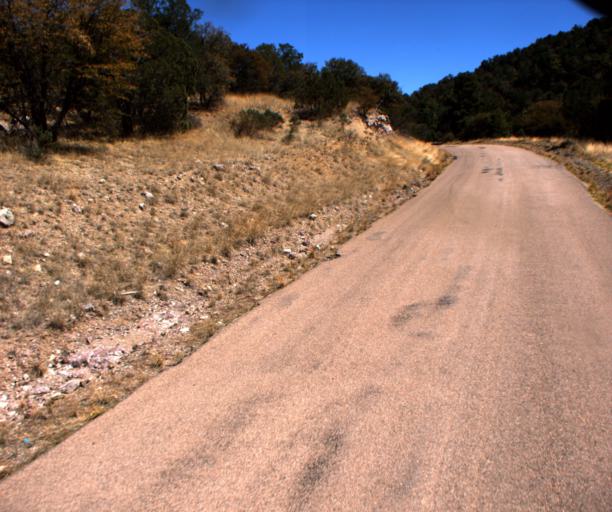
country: US
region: Arizona
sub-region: Cochise County
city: Sierra Vista
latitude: 31.4649
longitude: -110.4623
